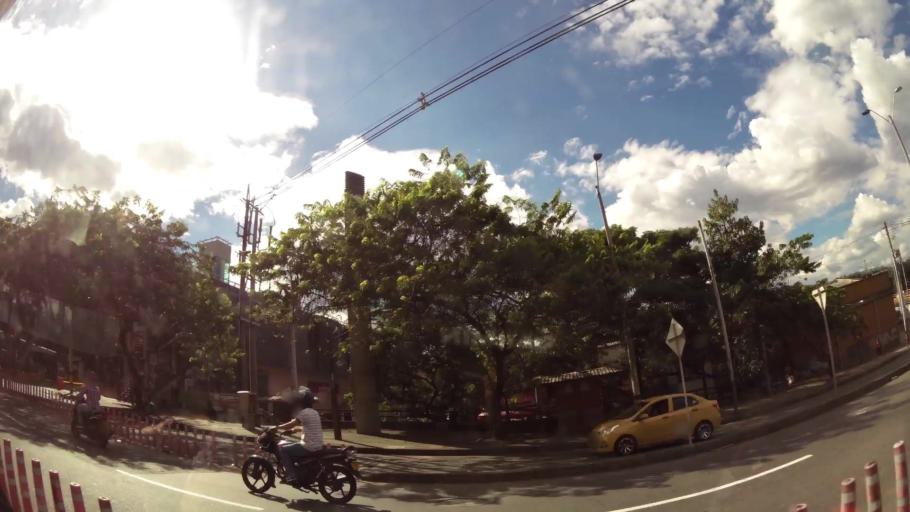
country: CO
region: Antioquia
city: Sabaneta
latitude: 6.1614
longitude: -75.6045
